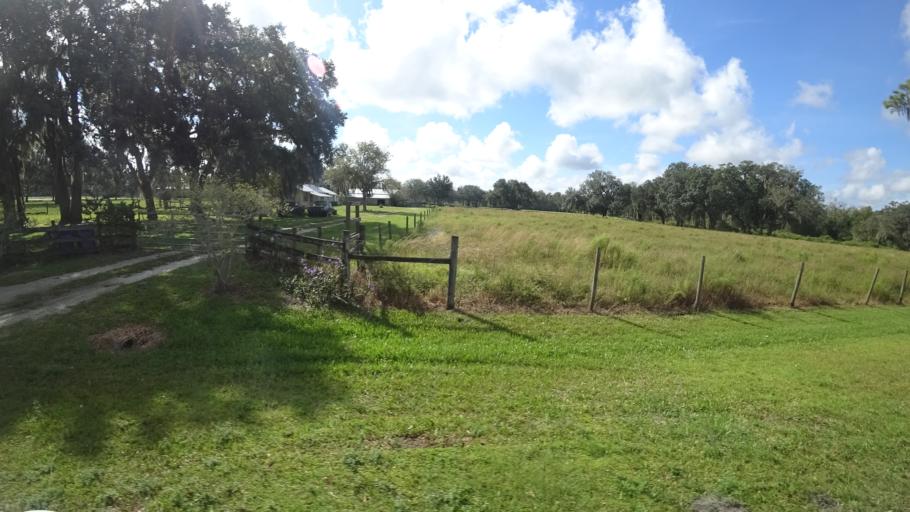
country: US
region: Florida
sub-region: Sarasota County
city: Lake Sarasota
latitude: 27.3393
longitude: -82.2010
